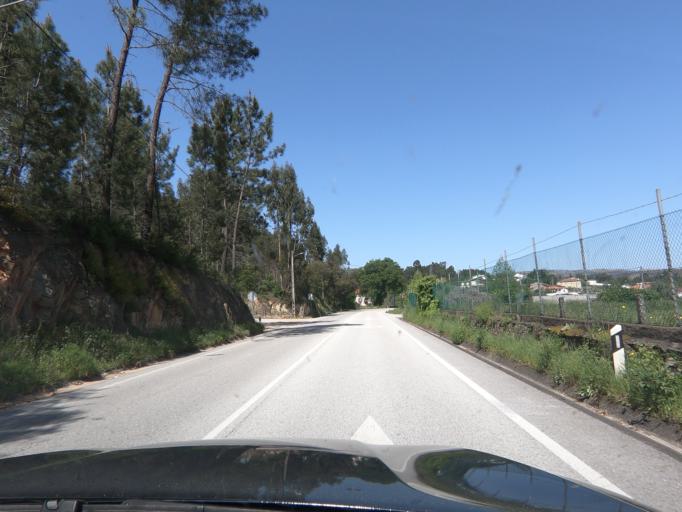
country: PT
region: Coimbra
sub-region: Vila Nova de Poiares
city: Poiares
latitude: 40.1868
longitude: -8.2567
